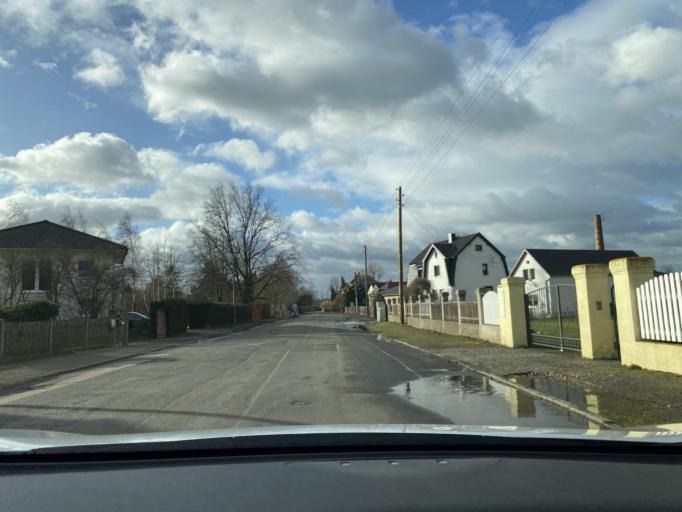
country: DE
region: Saxony
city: Zwenkau
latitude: 51.2605
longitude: 12.3052
